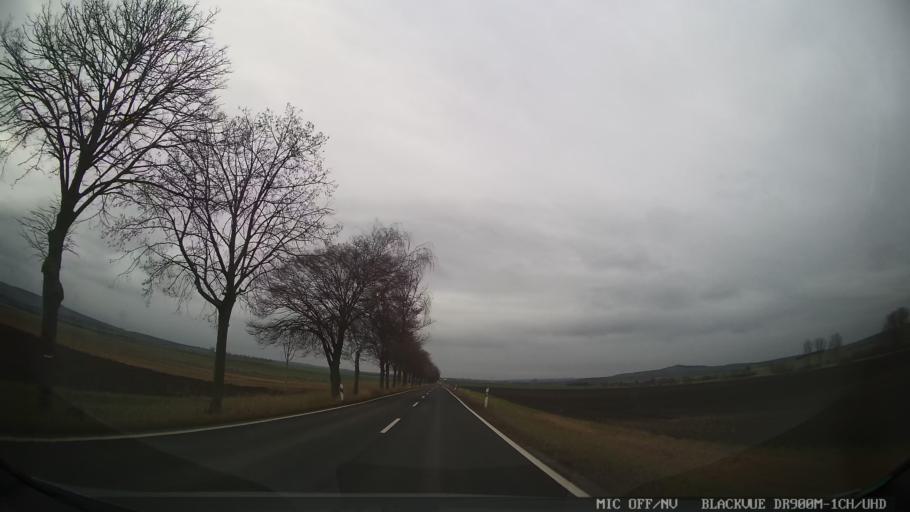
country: DE
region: Rheinland-Pfalz
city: Frettenheim
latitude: 49.7727
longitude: 8.2391
